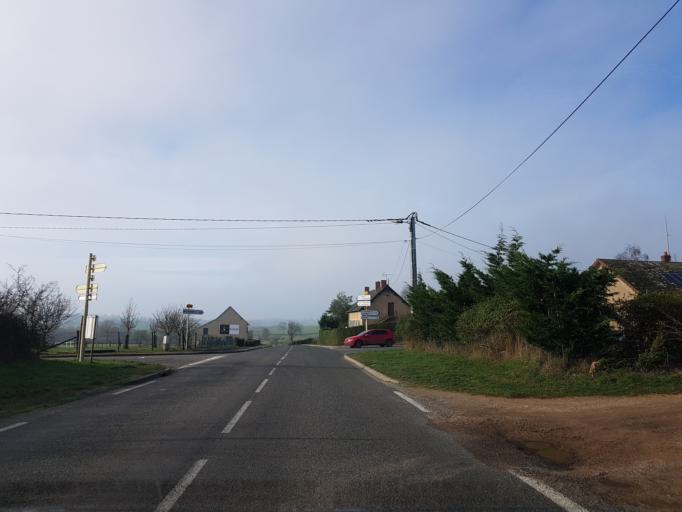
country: FR
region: Bourgogne
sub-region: Departement de Saone-et-Loire
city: Gueugnon
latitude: 46.5979
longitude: 3.9948
